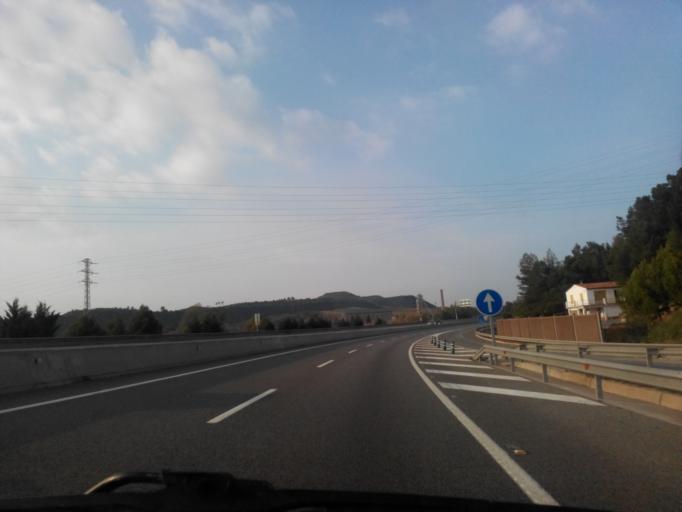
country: ES
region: Catalonia
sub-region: Provincia de Barcelona
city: Sallent
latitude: 41.8350
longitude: 1.8815
